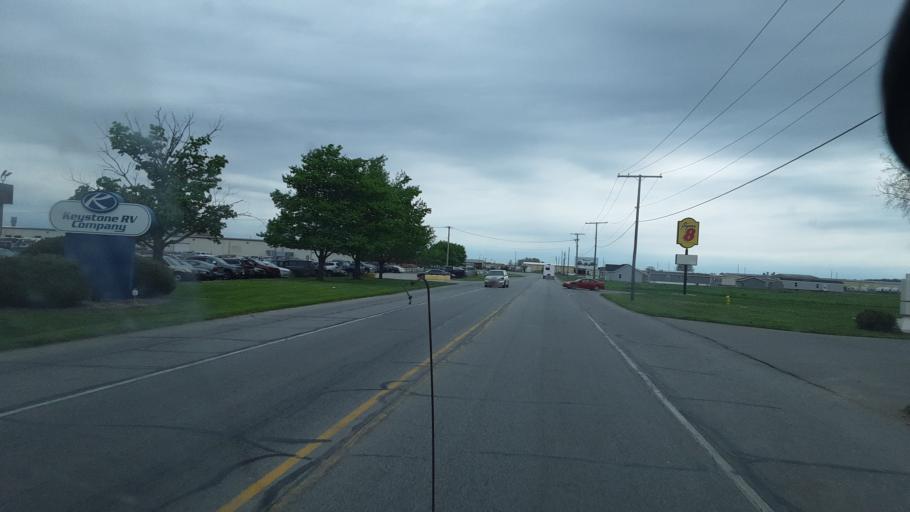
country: US
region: Indiana
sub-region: Elkhart County
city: New Paris
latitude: 41.5450
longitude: -85.7801
